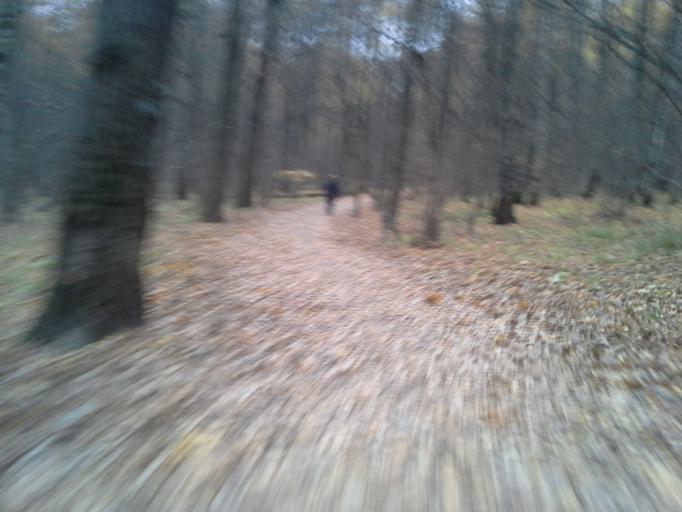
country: RU
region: Moscow
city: Chertanovo Yuzhnoye
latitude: 55.6173
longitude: 37.5741
